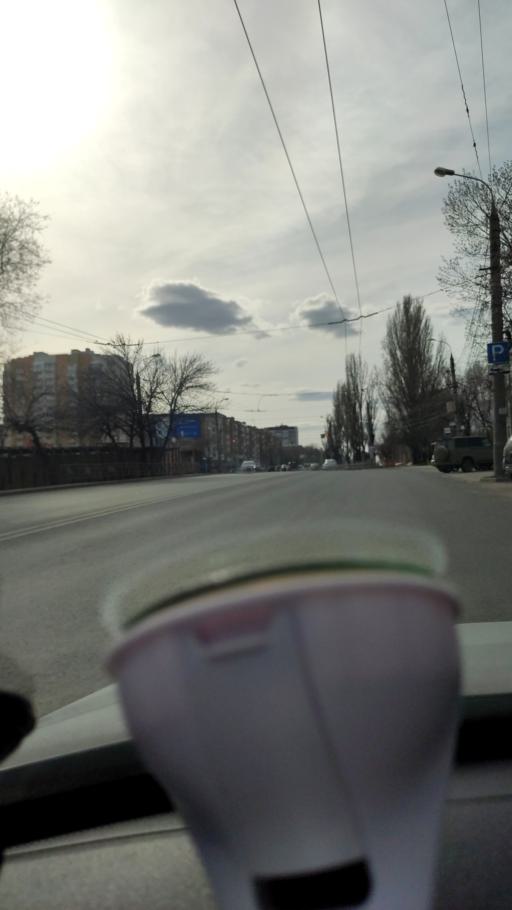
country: RU
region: Samara
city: Samara
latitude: 53.2134
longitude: 50.2154
